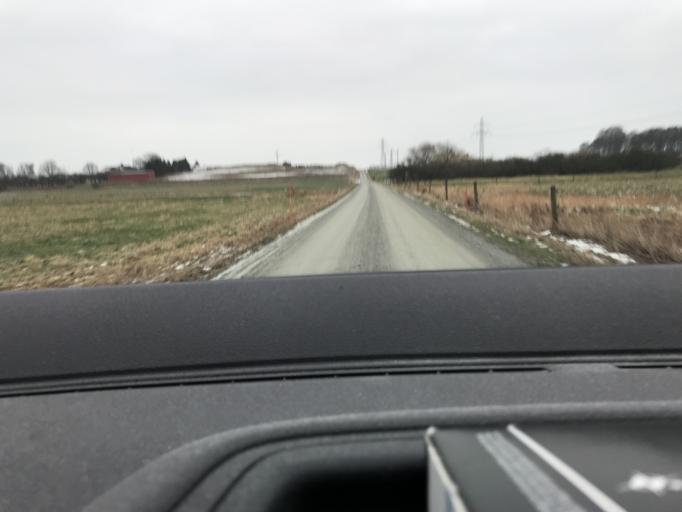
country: SE
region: Skane
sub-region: Ystads Kommun
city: Kopingebro
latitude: 55.4586
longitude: 13.8886
